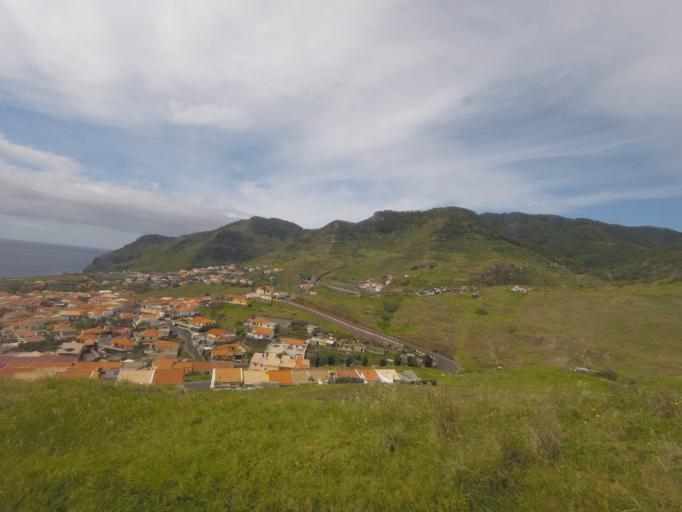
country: PT
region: Madeira
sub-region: Machico
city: Canical
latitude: 32.7418
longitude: -16.7368
